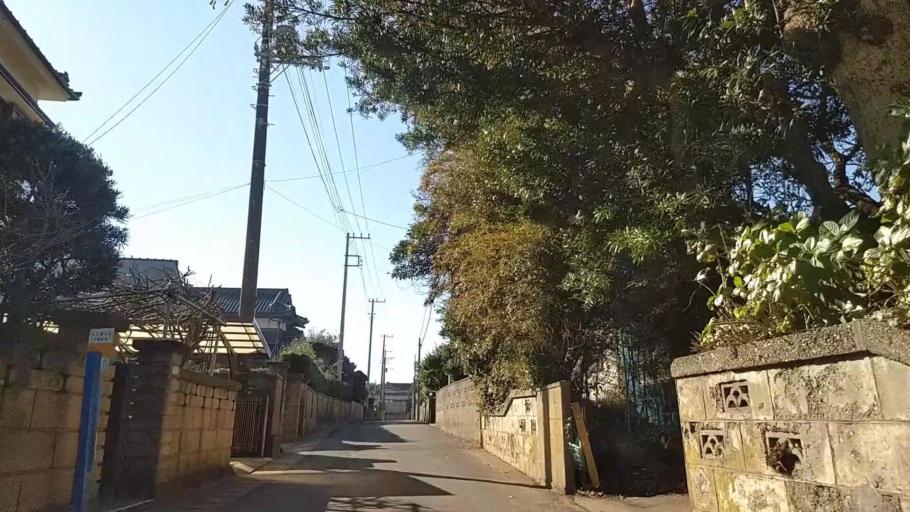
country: JP
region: Chiba
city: Hasaki
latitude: 35.7117
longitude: 140.8489
